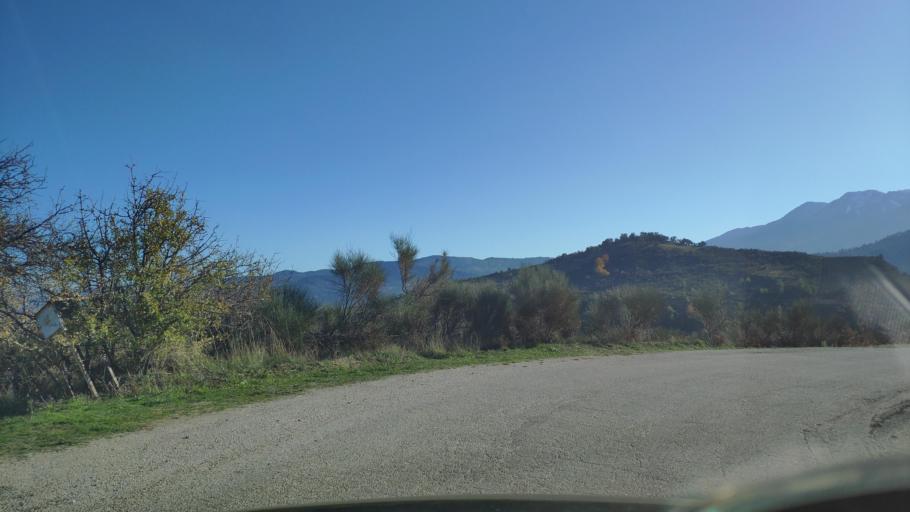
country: GR
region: Peloponnese
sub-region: Nomos Korinthias
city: Xylokastro
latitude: 38.0308
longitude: 22.4746
